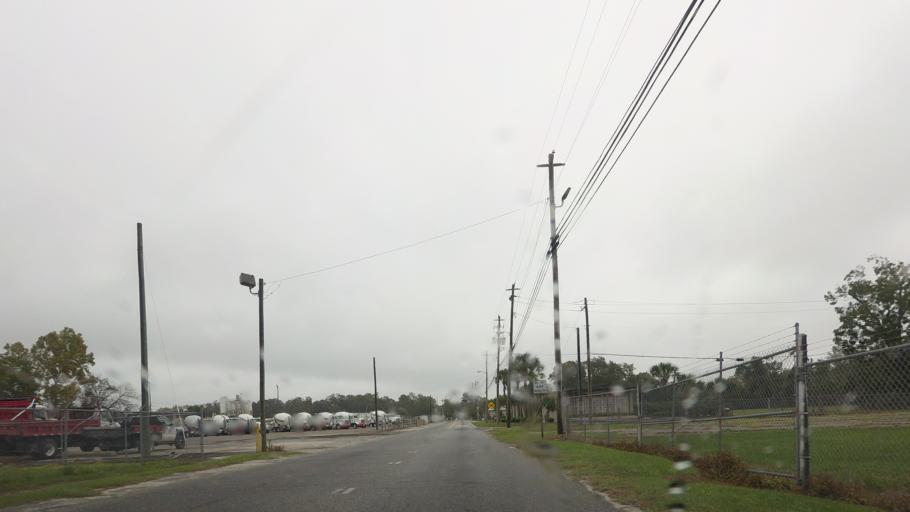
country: US
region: Georgia
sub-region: Lowndes County
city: Valdosta
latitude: 30.8302
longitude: -83.2950
